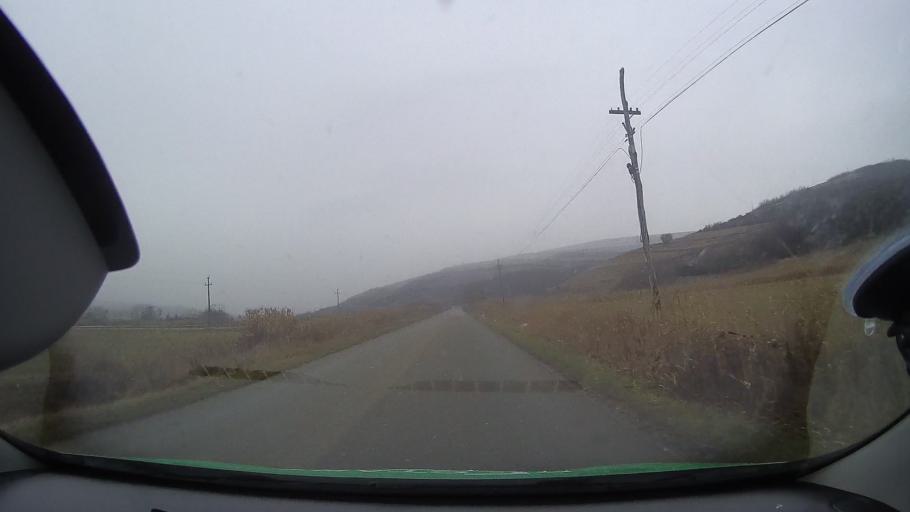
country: RO
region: Alba
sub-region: Comuna Farau
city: Farau
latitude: 46.3392
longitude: 23.9910
